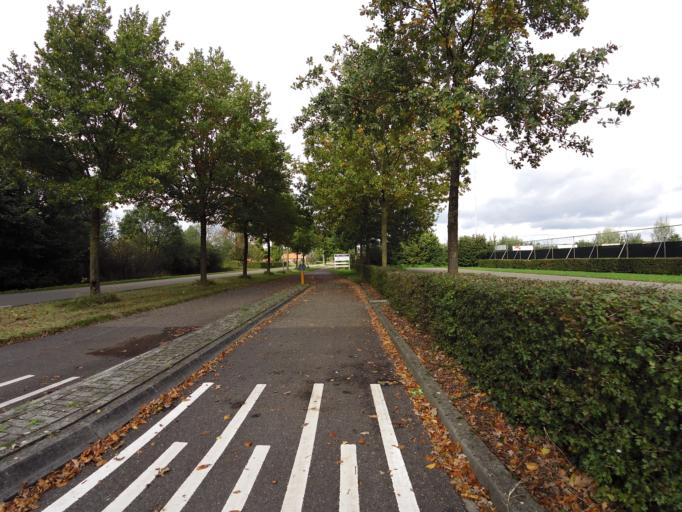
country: NL
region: Gelderland
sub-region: Gemeente Bronckhorst
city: Baak
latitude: 52.0816
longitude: 6.2636
